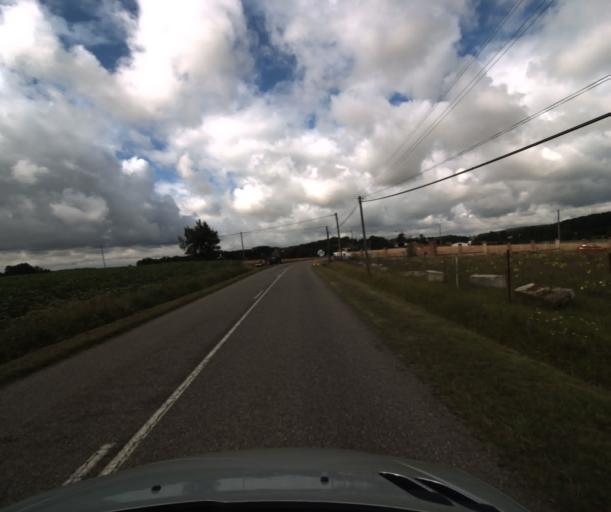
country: FR
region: Midi-Pyrenees
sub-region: Departement du Tarn-et-Garonne
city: Lavit
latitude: 43.9731
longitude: 0.9510
